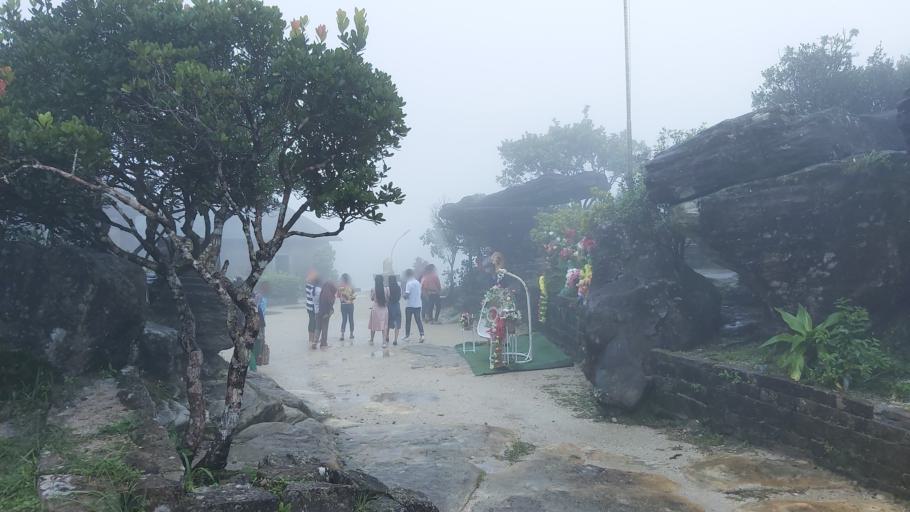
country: KH
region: Kampot
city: Kampot
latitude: 10.6297
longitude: 104.0176
